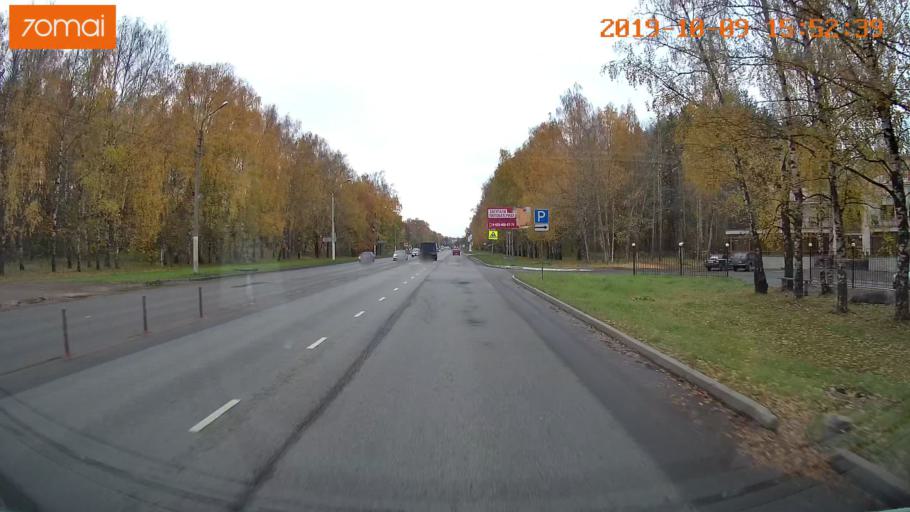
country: RU
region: Kostroma
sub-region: Kostromskoy Rayon
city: Kostroma
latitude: 57.7879
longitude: 40.9654
